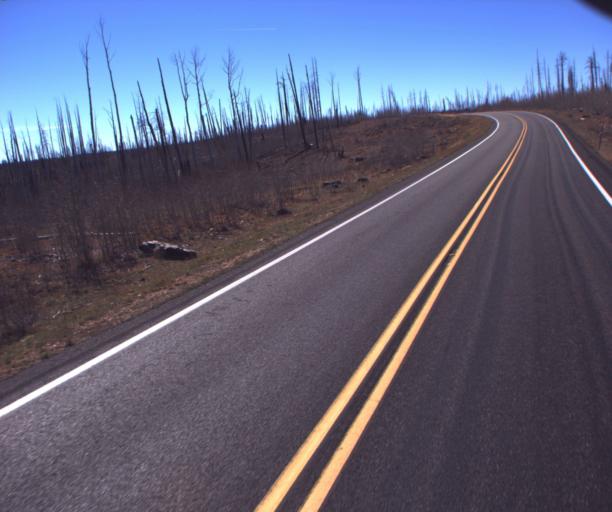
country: US
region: Arizona
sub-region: Coconino County
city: Grand Canyon
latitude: 36.5577
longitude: -112.1718
